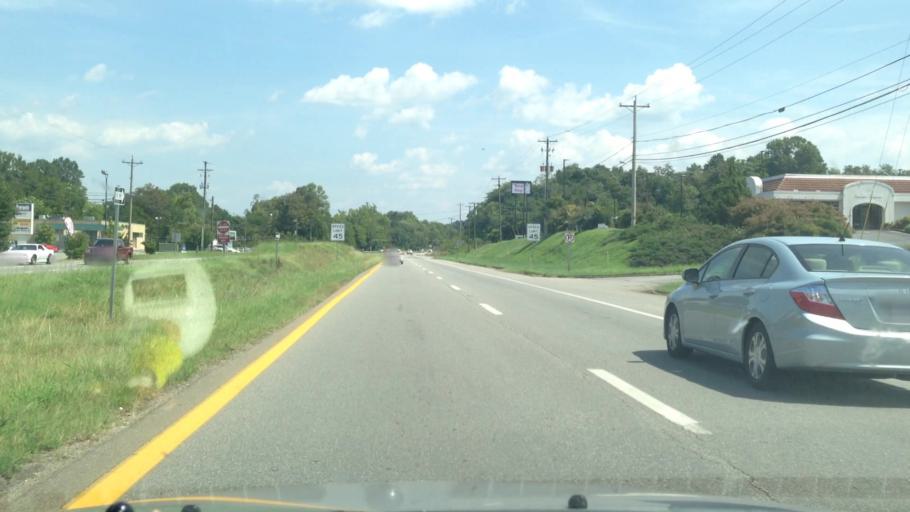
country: US
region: Virginia
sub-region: City of Martinsville
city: Martinsville
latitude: 36.6530
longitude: -79.8742
